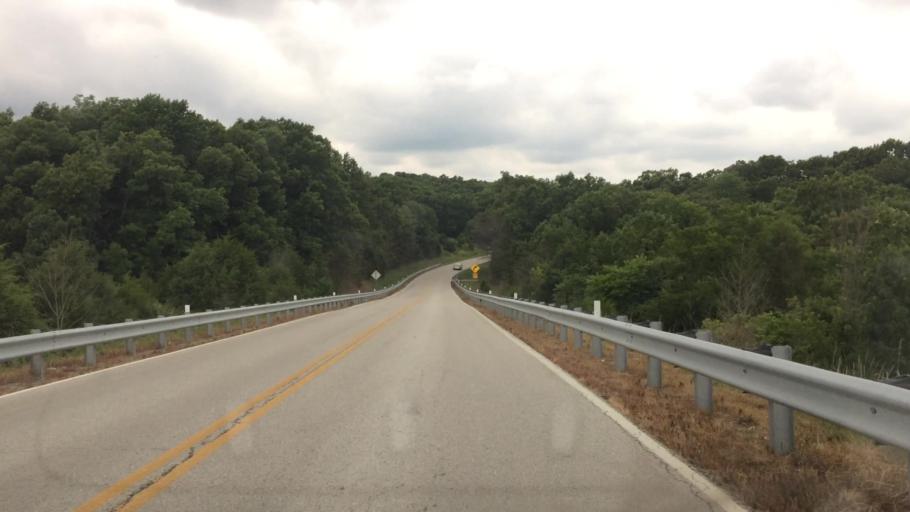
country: US
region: Missouri
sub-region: Webster County
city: Marshfield
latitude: 37.3040
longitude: -93.0006
